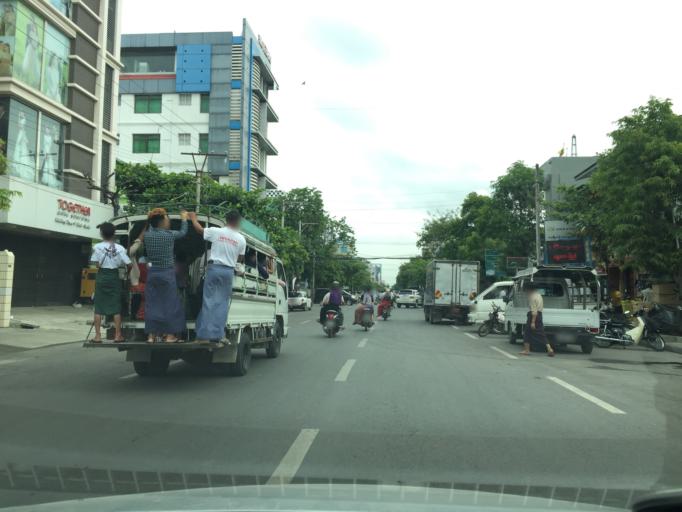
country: MM
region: Mandalay
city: Mandalay
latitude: 21.9737
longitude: 96.0789
